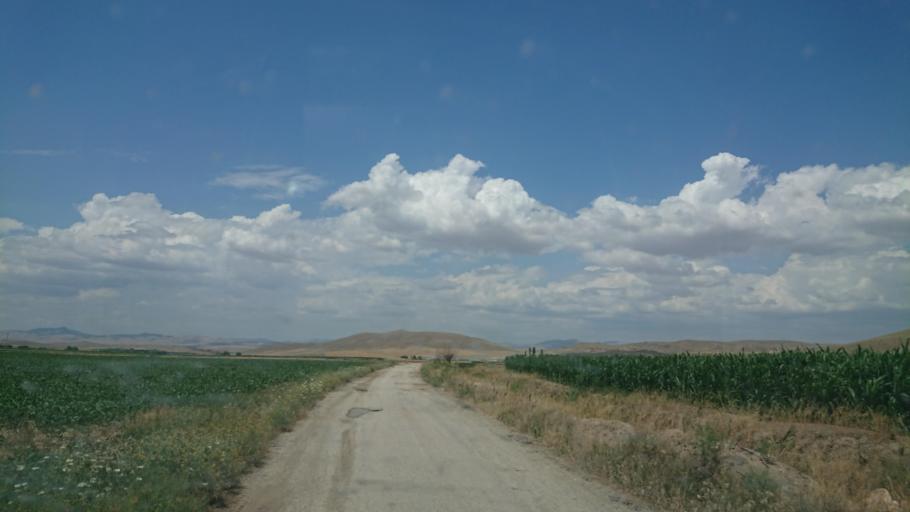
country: TR
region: Aksaray
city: Sariyahsi
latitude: 38.9838
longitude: 33.9074
